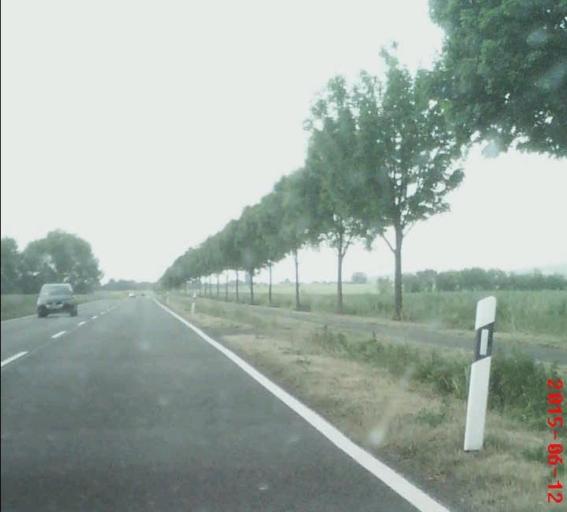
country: DE
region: Saxony-Anhalt
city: Bennungen
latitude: 51.4593
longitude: 11.1502
